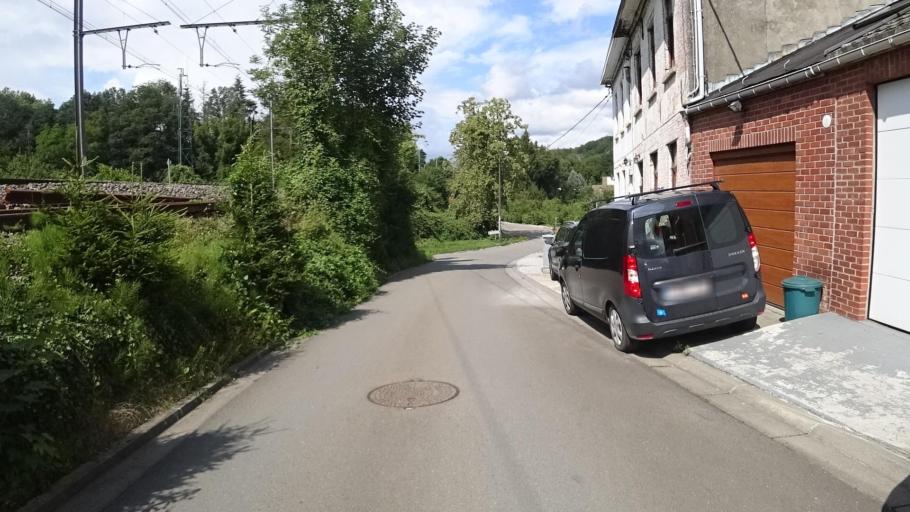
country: BE
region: Wallonia
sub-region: Province du Brabant Wallon
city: Villers-la-Ville
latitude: 50.5831
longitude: 4.5288
